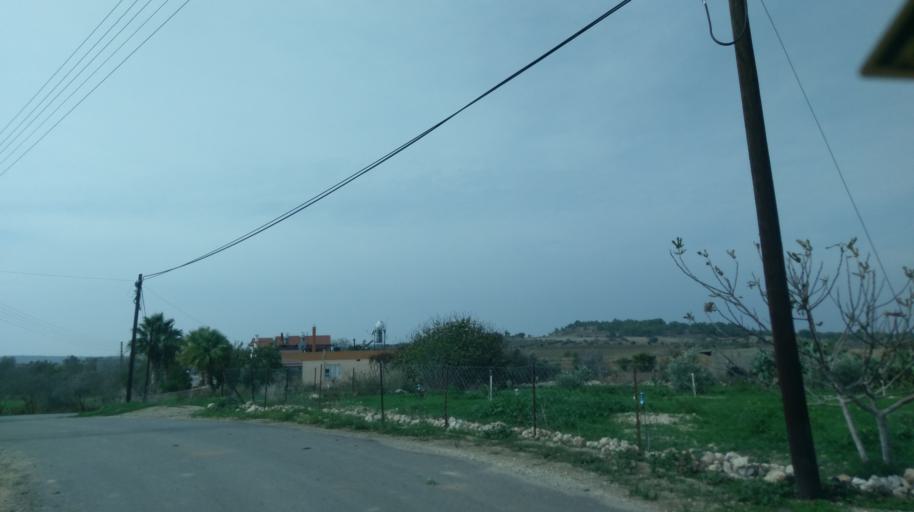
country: CY
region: Keryneia
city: Lapithos
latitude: 35.3021
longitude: 33.1047
